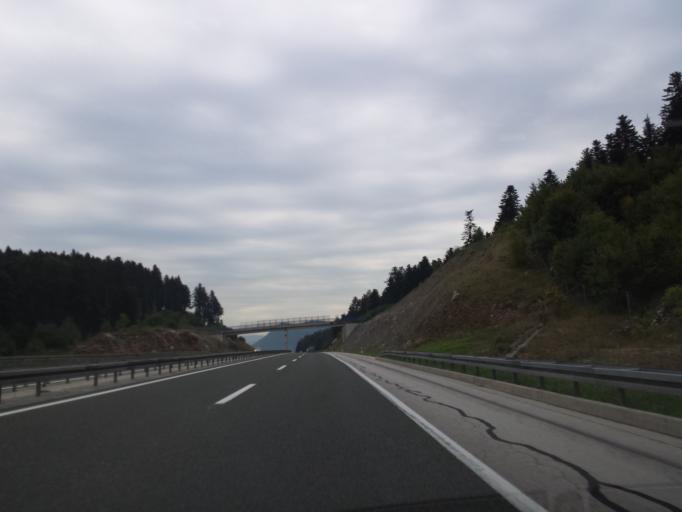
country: HR
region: Licko-Senjska
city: Otocac
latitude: 44.8506
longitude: 15.2299
